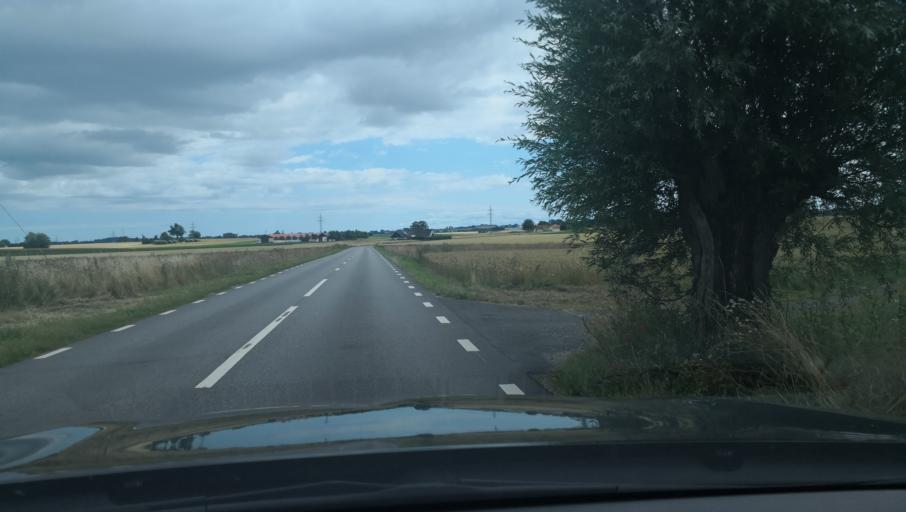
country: SE
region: Skane
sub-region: Tomelilla Kommun
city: Tomelilla
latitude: 55.5208
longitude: 14.1312
